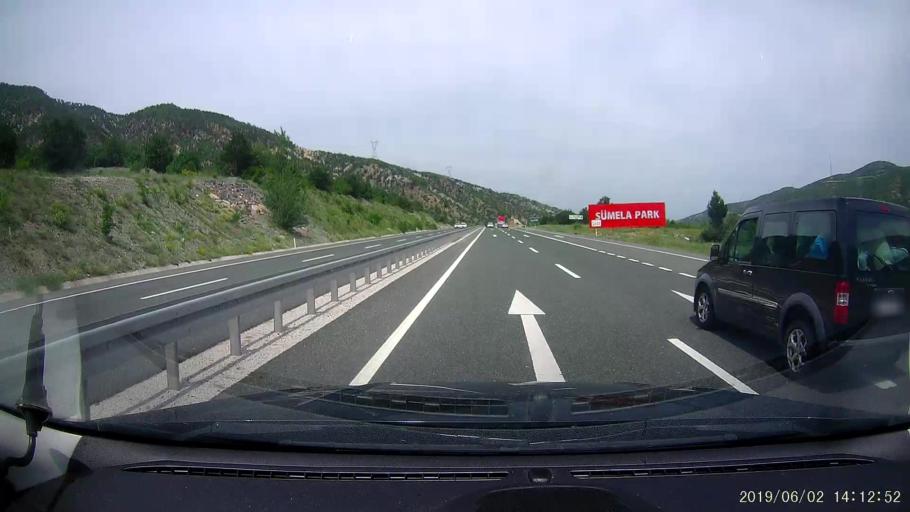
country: TR
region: Cankiri
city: Yaprakli
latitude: 40.9197
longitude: 33.8170
